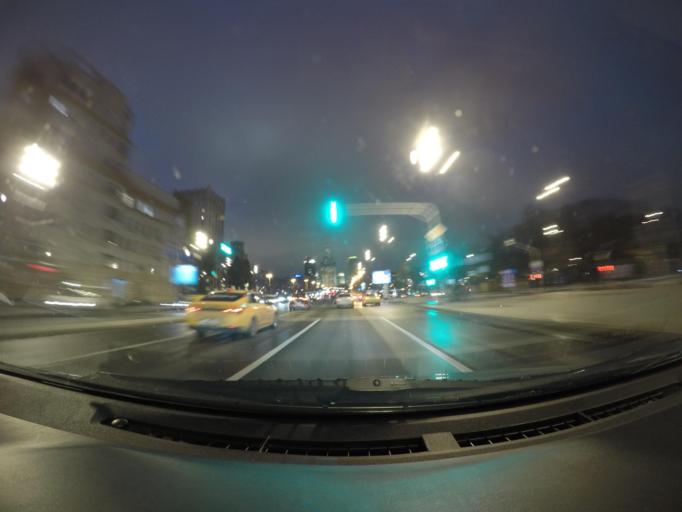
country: RU
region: Moskovskaya
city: Dorogomilovo
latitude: 55.7454
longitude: 37.5689
